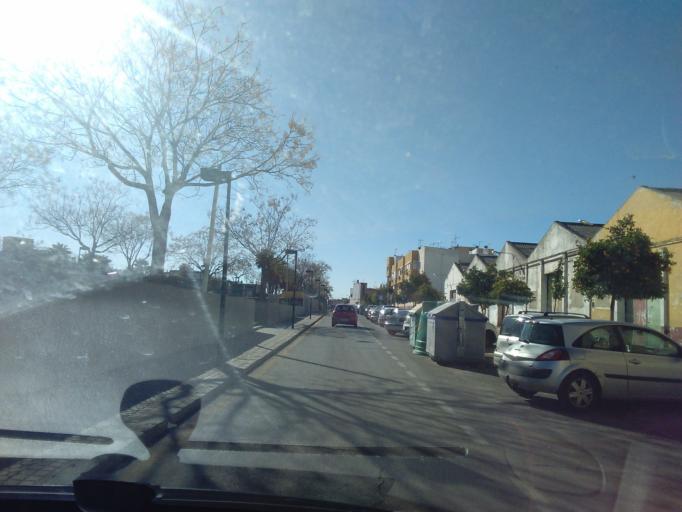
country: ES
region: Andalusia
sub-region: Provincia de Sevilla
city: Sevilla
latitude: 37.3875
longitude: -5.9092
